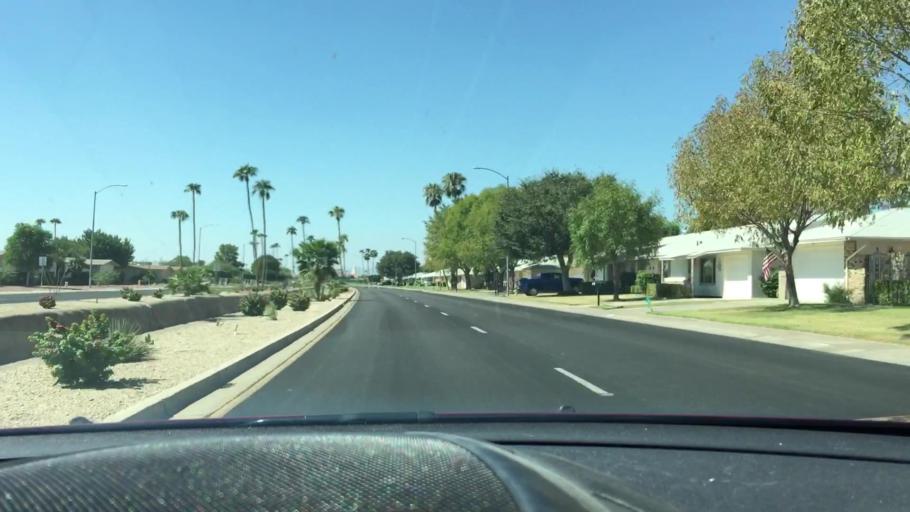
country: US
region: Arizona
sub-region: Maricopa County
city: Sun City
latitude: 33.6459
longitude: -112.2790
